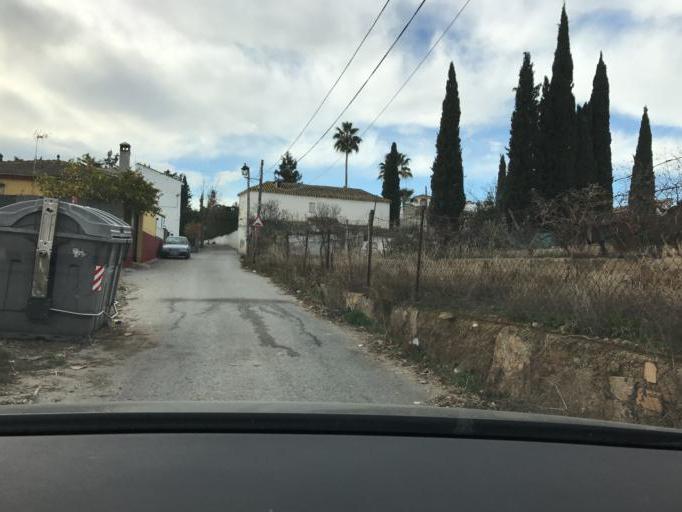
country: ES
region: Andalusia
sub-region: Provincia de Granada
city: Ogijares
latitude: 37.1176
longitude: -3.6144
